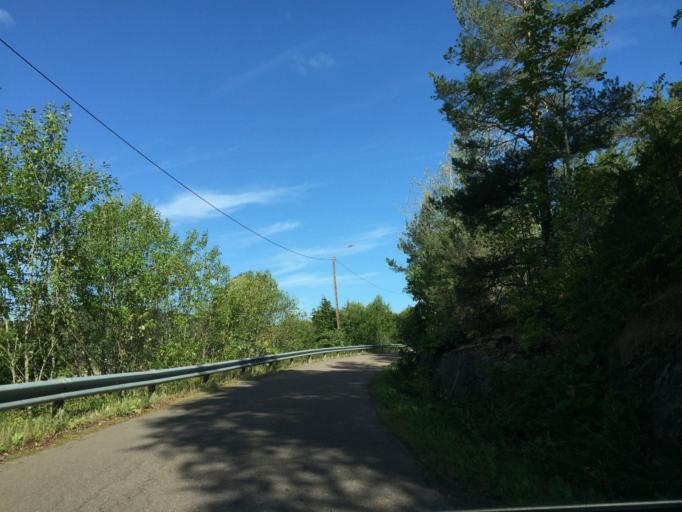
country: NO
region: Vestfold
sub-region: Holmestrand
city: Gullhaug
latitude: 59.4793
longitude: 10.1771
